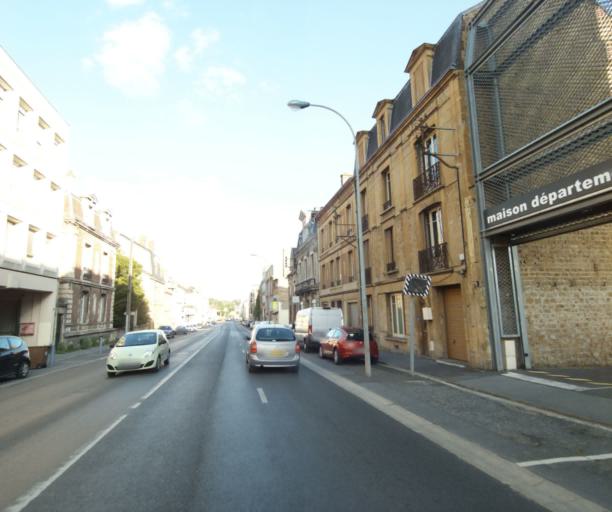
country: FR
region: Champagne-Ardenne
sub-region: Departement des Ardennes
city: Charleville-Mezieres
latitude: 49.7681
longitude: 4.7160
